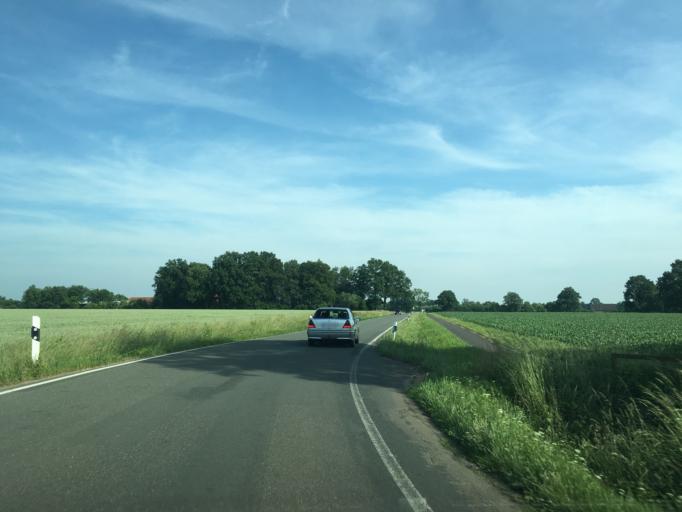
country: DE
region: North Rhine-Westphalia
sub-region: Regierungsbezirk Munster
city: Nordwalde
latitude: 52.1096
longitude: 7.4620
